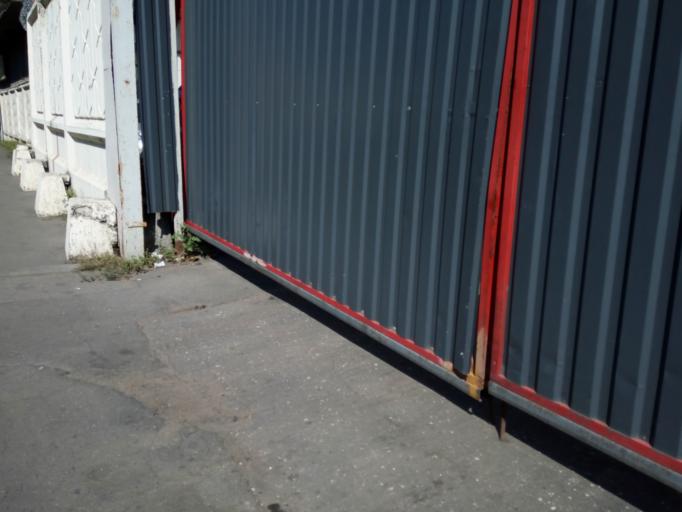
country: RU
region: Moscow
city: Sokol
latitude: 55.7712
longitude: 37.5183
